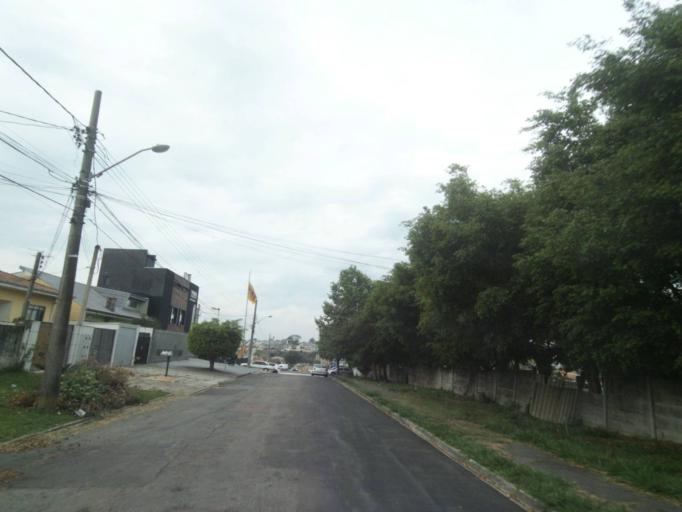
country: BR
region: Parana
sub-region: Pinhais
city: Pinhais
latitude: -25.4722
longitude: -49.2304
